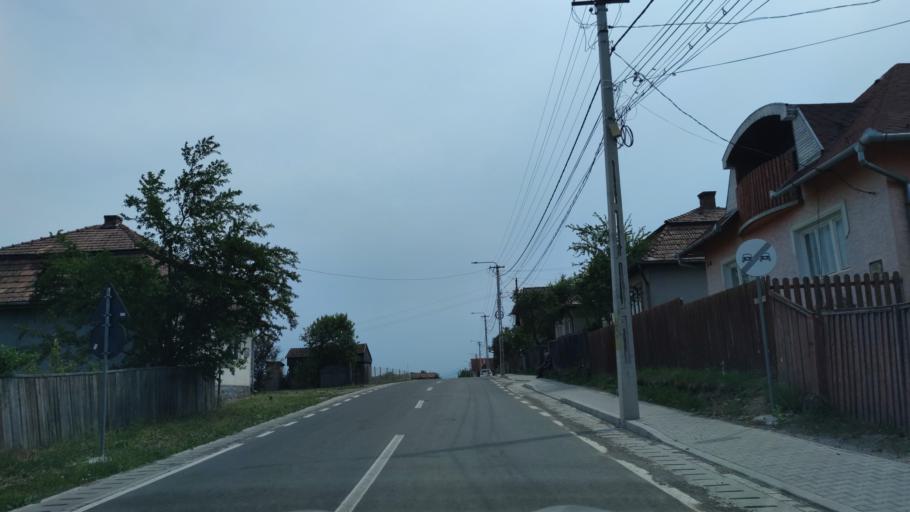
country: RO
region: Harghita
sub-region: Comuna Remetea
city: Remetea
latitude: 46.8099
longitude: 25.4595
